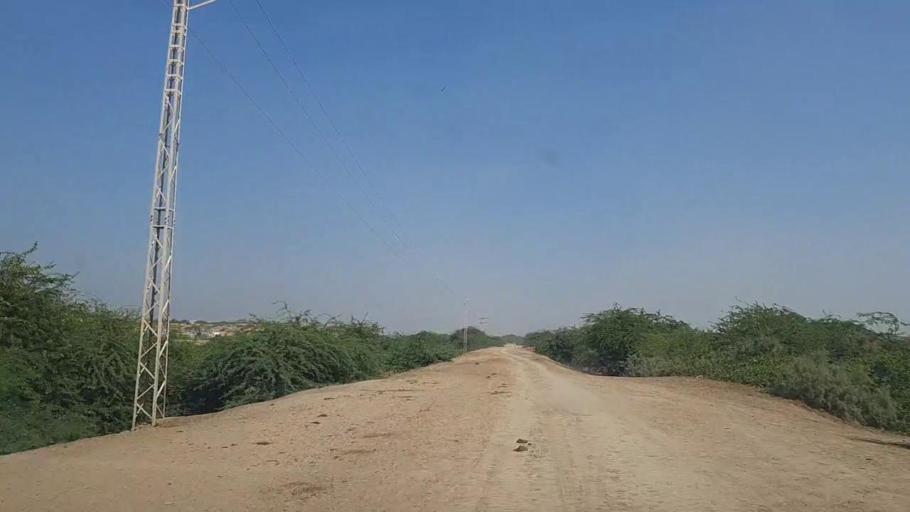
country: PK
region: Sindh
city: Daro Mehar
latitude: 24.8898
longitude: 68.0632
